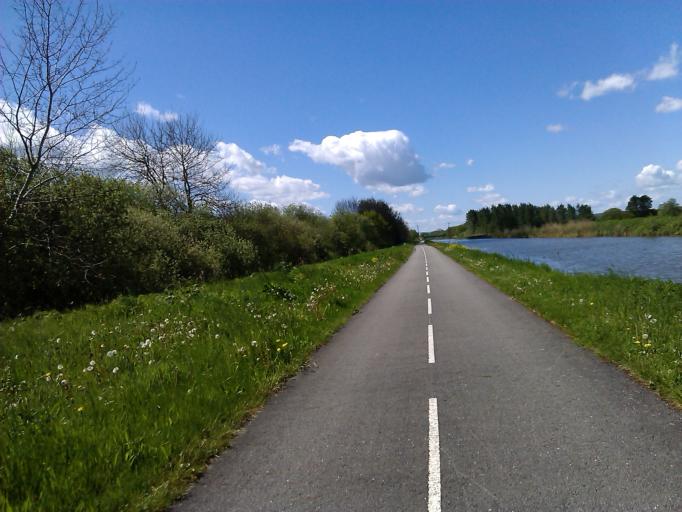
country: FR
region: Franche-Comte
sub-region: Territoire de Belfort
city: Montreux-Chateau
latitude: 47.5877
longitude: 6.9747
